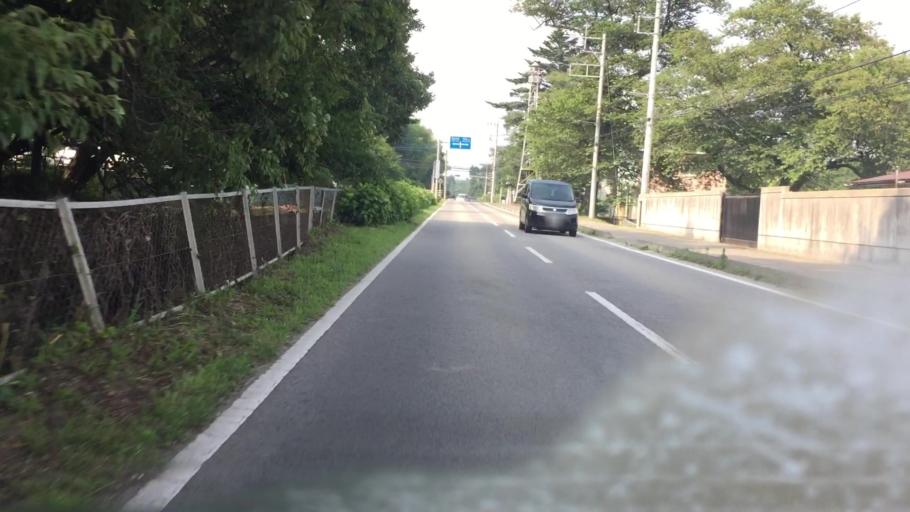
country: JP
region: Tochigi
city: Kuroiso
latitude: 36.9930
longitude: 139.9931
